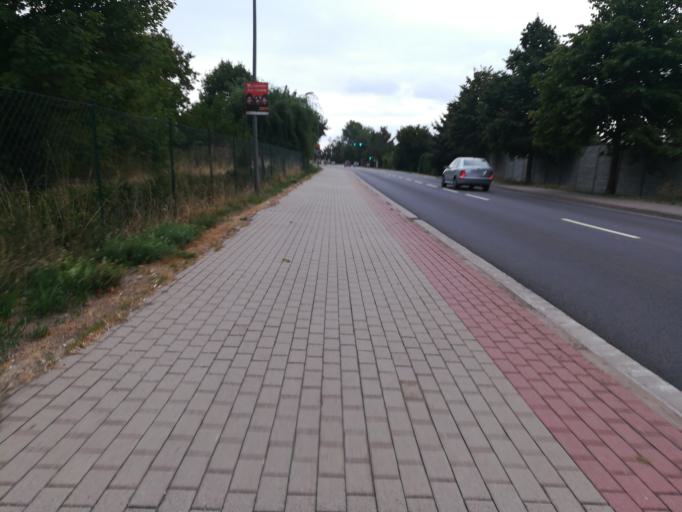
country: DE
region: Saxony-Anhalt
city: Irxleben
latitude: 52.1633
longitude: 11.4891
